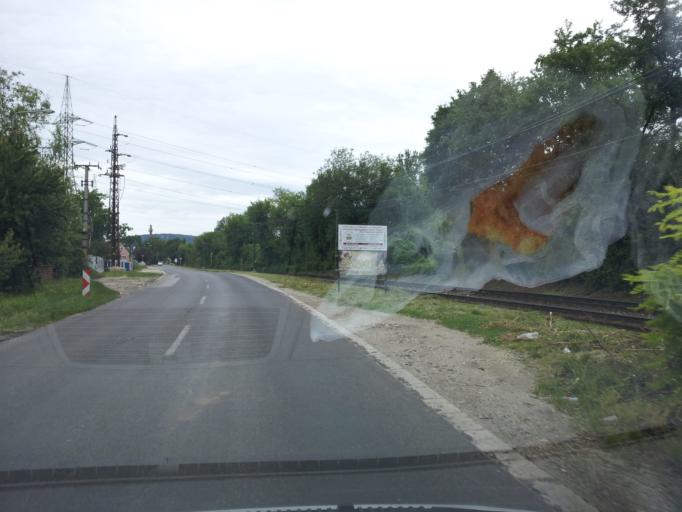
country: HU
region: Pest
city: Pomaz
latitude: 47.6362
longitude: 19.0396
